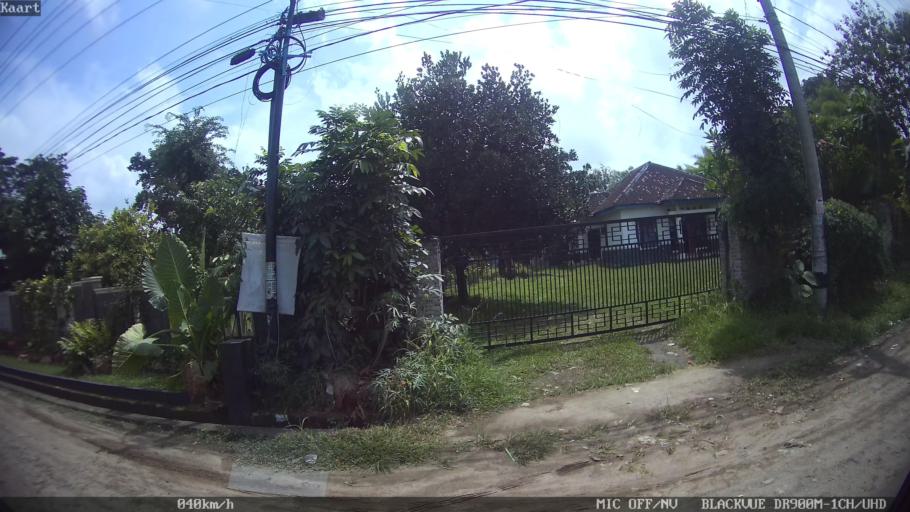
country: ID
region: Lampung
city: Kedaton
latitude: -5.3589
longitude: 105.3028
